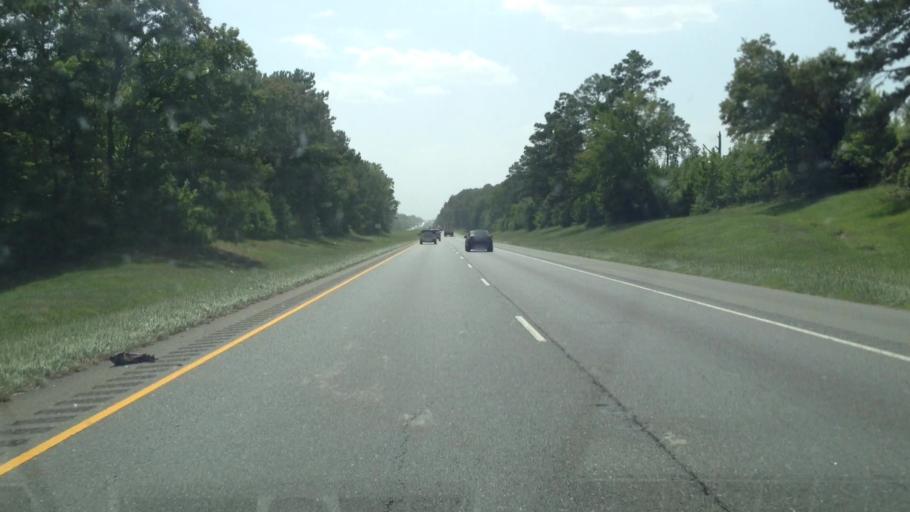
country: US
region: Louisiana
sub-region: Bossier Parish
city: Eastwood
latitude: 32.5423
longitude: -93.5636
